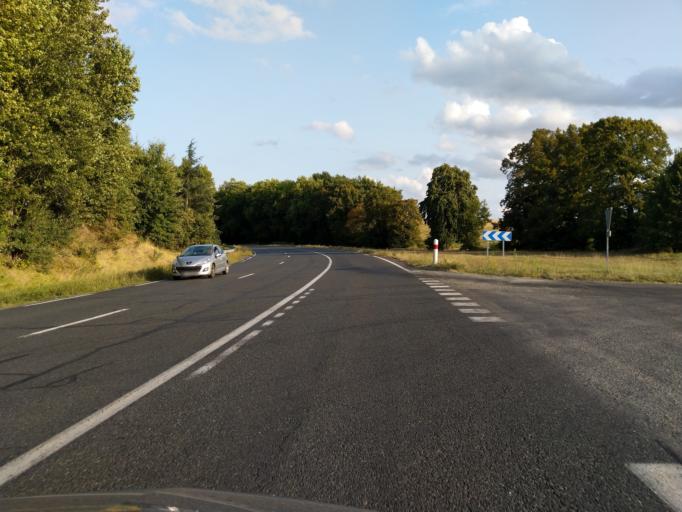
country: FR
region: Midi-Pyrenees
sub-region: Departement du Tarn
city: Realmont
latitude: 43.8025
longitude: 2.1831
